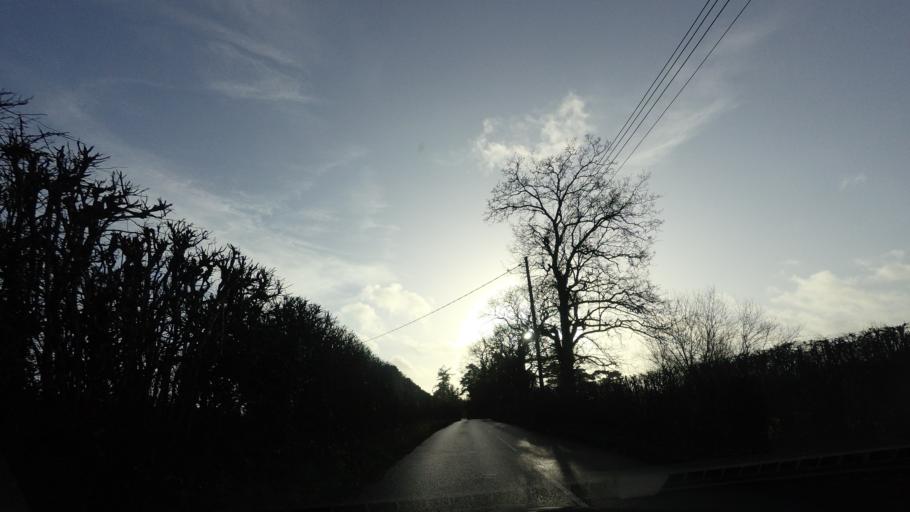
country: GB
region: England
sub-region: Kent
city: Borough Green
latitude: 51.2747
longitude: 0.2847
